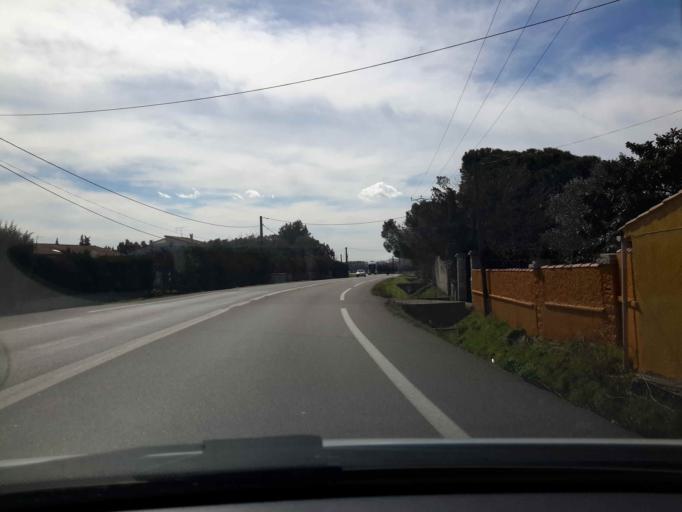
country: FR
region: Languedoc-Roussillon
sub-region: Departement du Gard
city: Vauvert
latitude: 43.7069
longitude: 4.2620
